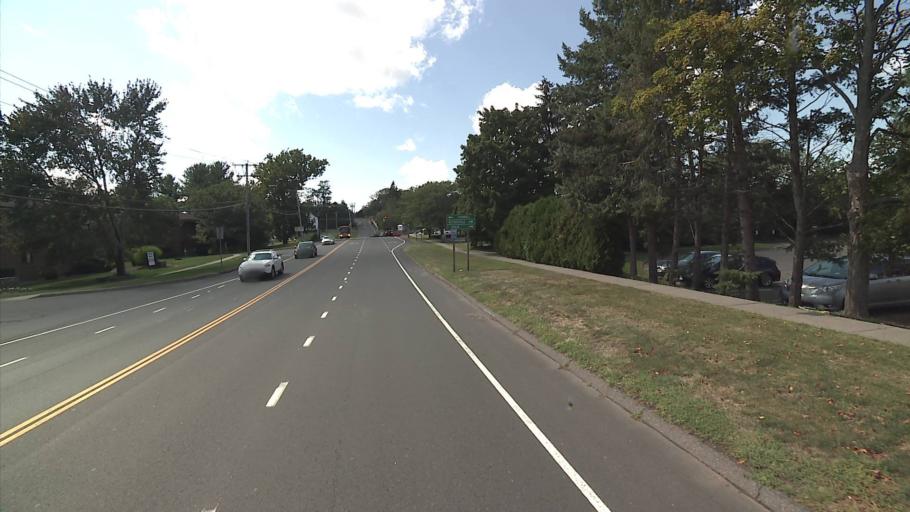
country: US
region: Connecticut
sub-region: Hartford County
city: Wethersfield
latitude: 41.6584
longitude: -72.6768
